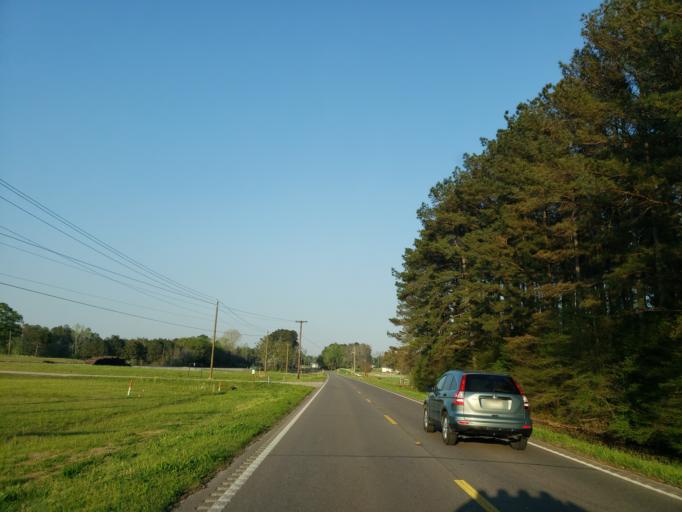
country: US
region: Mississippi
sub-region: Lauderdale County
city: Marion
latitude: 32.3970
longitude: -88.6120
